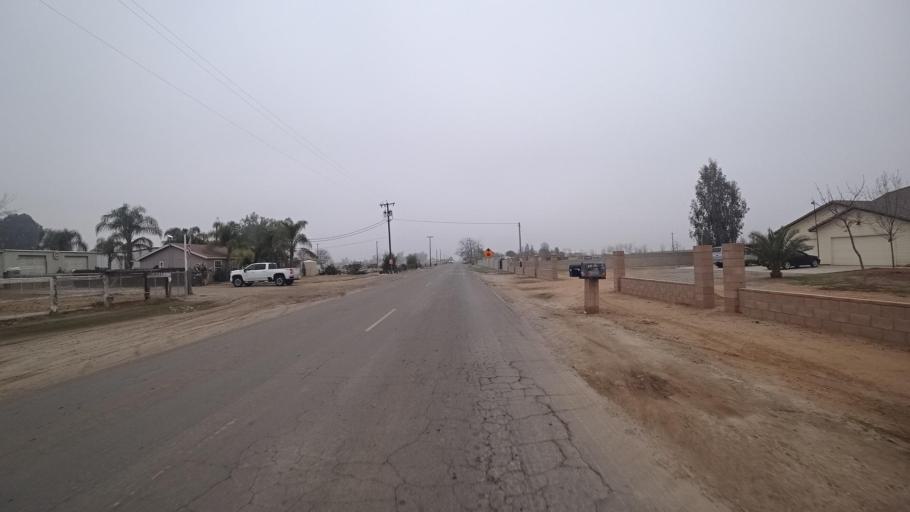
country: US
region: California
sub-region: Kern County
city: Greenfield
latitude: 35.2380
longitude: -119.0906
